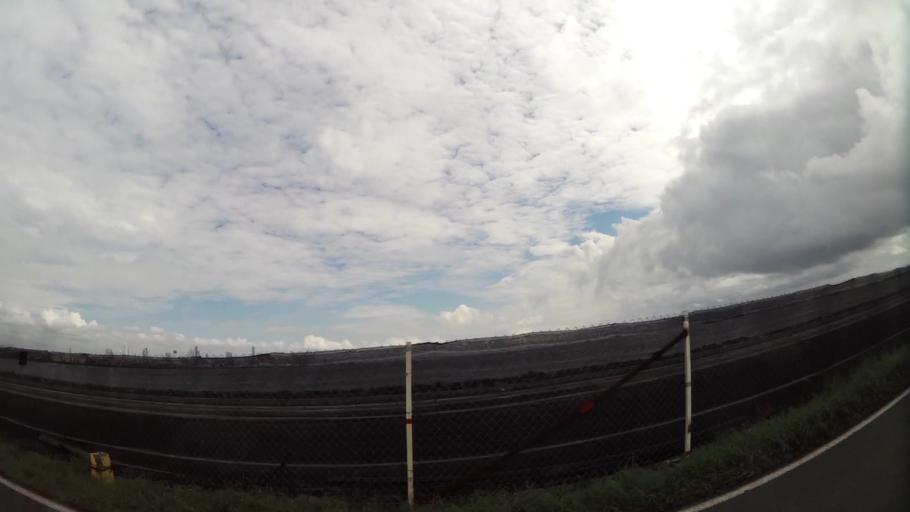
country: PA
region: Panama
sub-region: Distrito de Panama
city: Ancon
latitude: 8.9277
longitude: -79.5421
